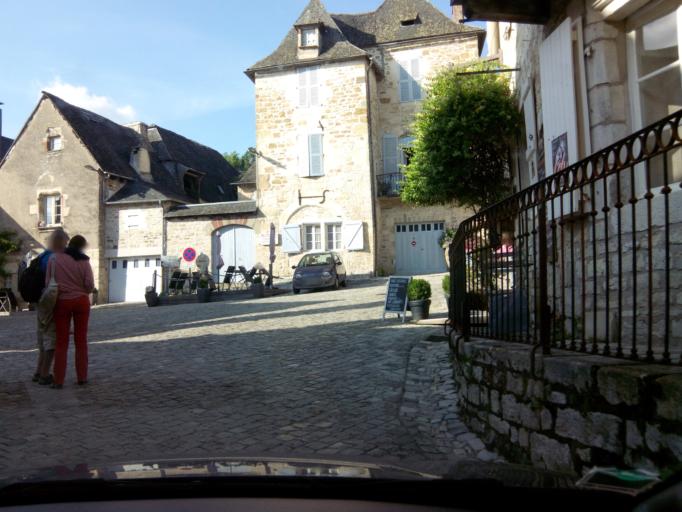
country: FR
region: Limousin
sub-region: Departement de la Correze
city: Cosnac
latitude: 45.0539
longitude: 1.5822
